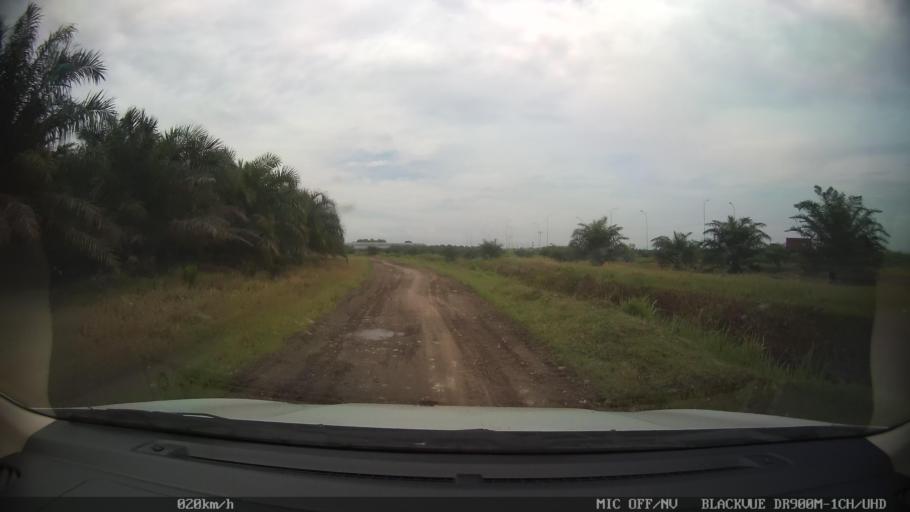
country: ID
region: North Sumatra
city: Sunggal
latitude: 3.6303
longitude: 98.5813
